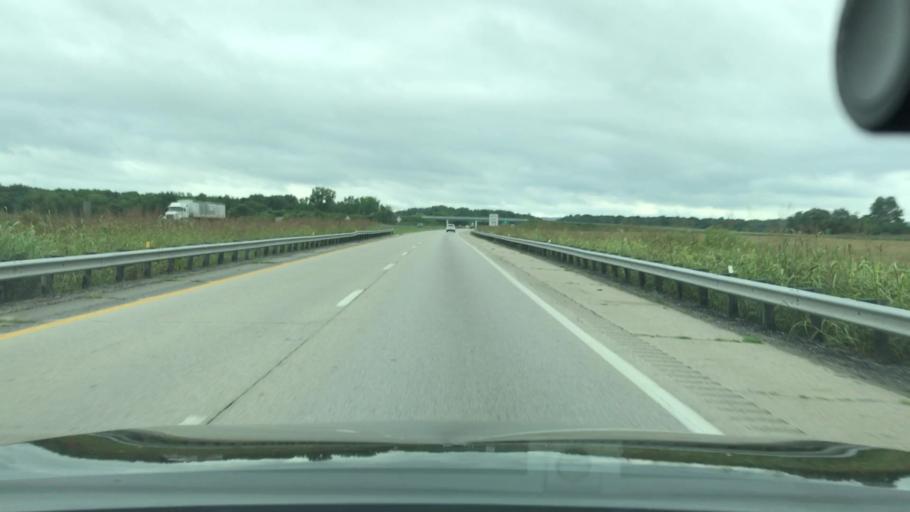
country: US
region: Ohio
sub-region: Ross County
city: Chillicothe
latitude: 39.3184
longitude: -82.9355
